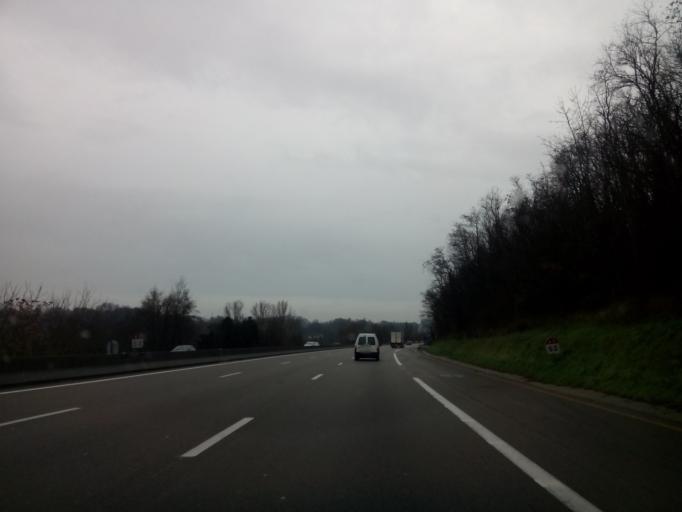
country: FR
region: Rhone-Alpes
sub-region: Departement de la Drome
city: Mercurol
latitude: 45.0927
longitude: 4.8790
